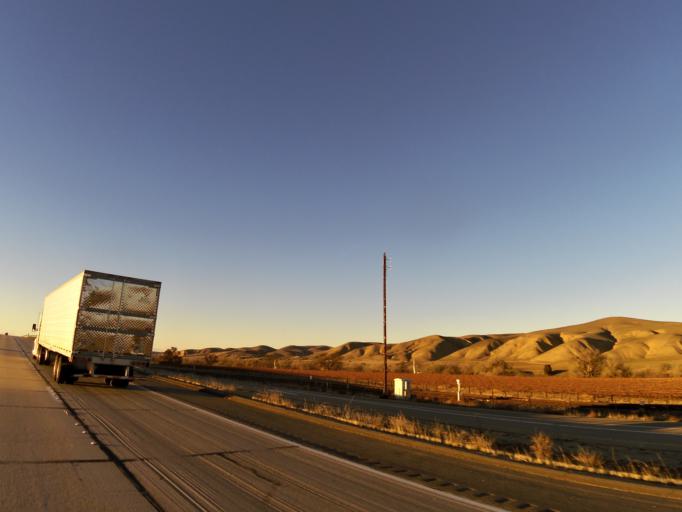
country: US
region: California
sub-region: San Luis Obispo County
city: San Miguel
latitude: 35.7736
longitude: -120.7099
